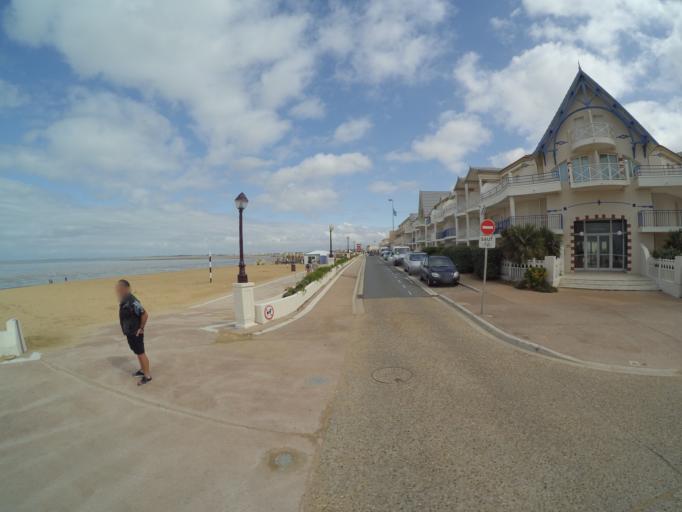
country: FR
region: Poitou-Charentes
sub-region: Departement de la Charente-Maritime
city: Chatelaillon-Plage
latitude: 46.0751
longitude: -1.0936
